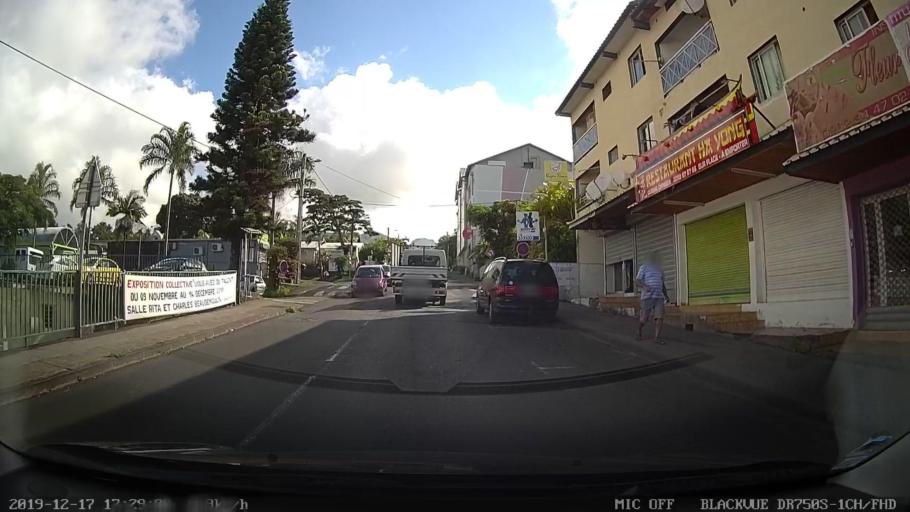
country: RE
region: Reunion
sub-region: Reunion
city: Le Tampon
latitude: -21.2801
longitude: 55.5134
